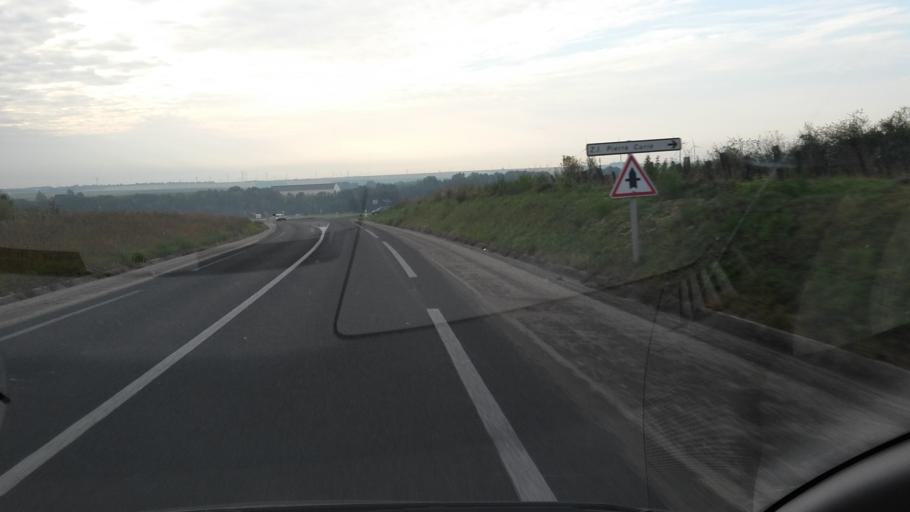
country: FR
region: Champagne-Ardenne
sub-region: Departement de la Marne
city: Fere-Champenoise
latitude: 48.7665
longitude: 3.9957
